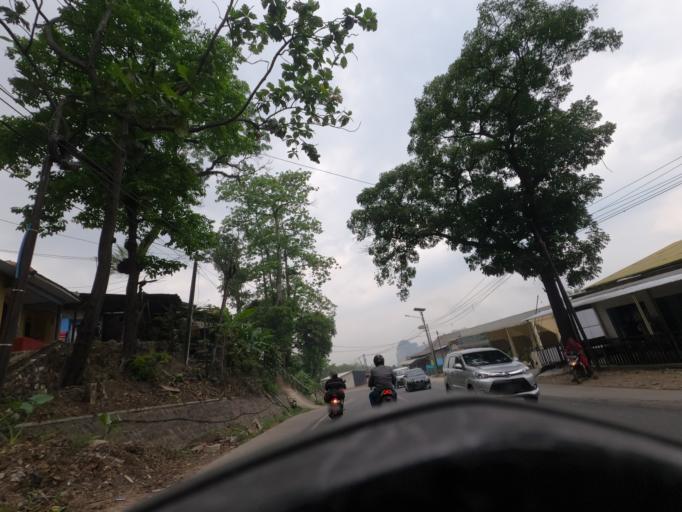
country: ID
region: West Java
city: Padalarang
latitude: -6.8326
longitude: 107.4370
